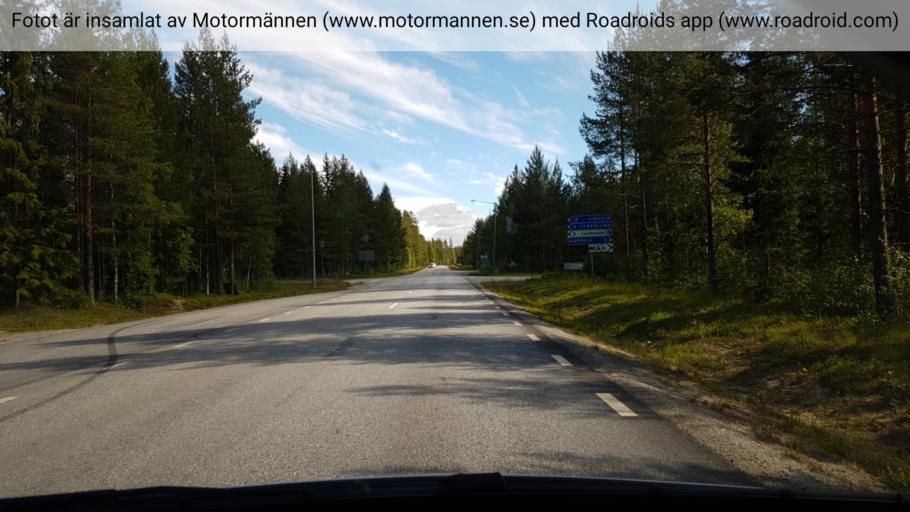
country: SE
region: Vaesterbotten
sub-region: Vindelns Kommun
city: Vindeln
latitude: 64.0850
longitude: 19.6258
